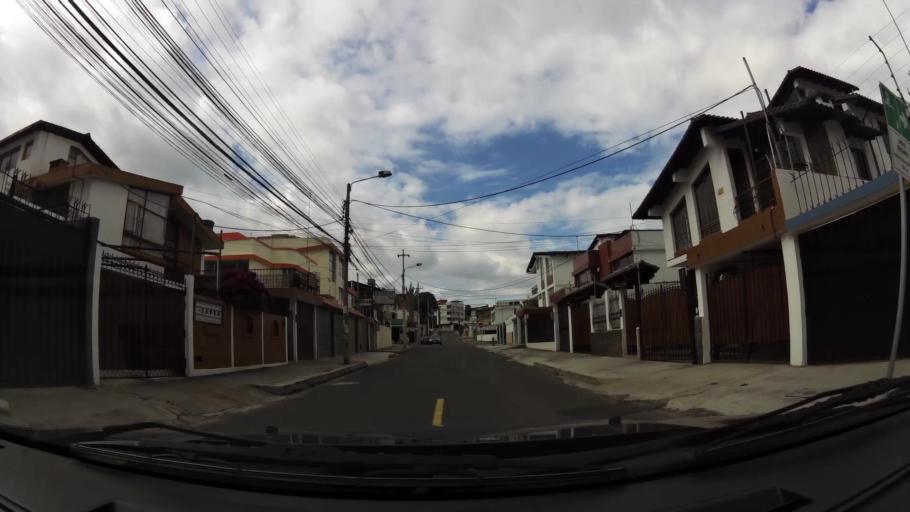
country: EC
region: Pichincha
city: Quito
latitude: -0.1601
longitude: -78.4809
